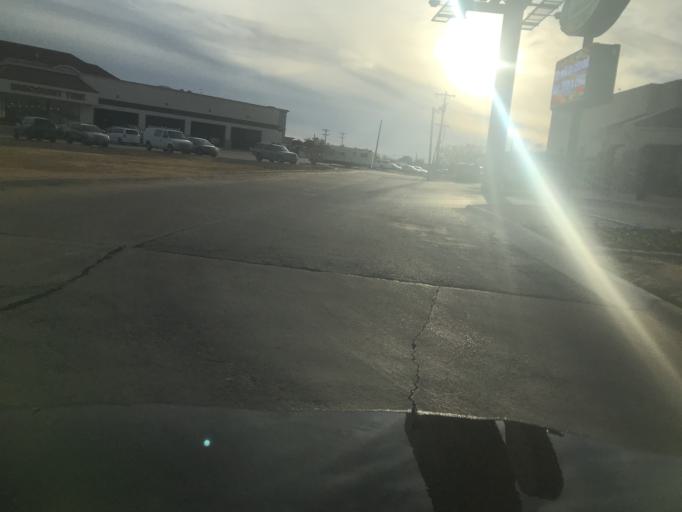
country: US
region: Texas
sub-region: Taylor County
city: Abilene
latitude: 32.4150
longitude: -99.7782
